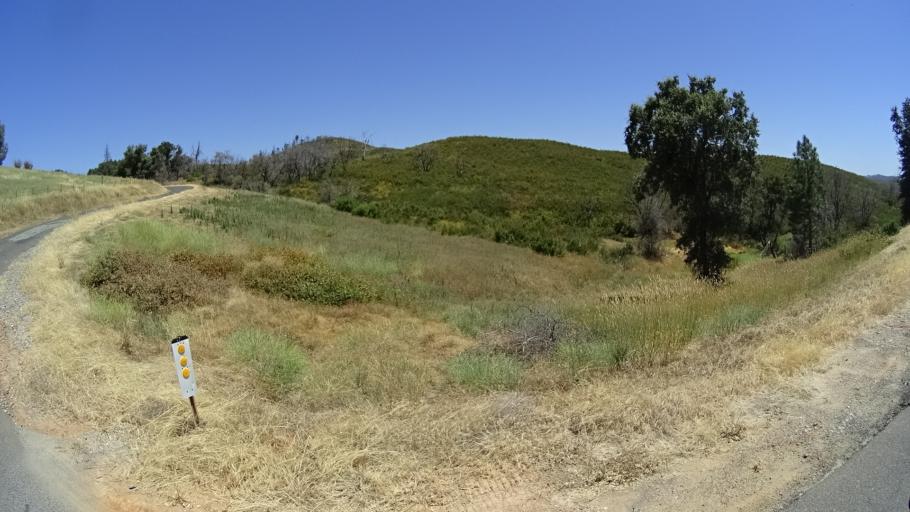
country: US
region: California
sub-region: Calaveras County
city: Mountain Ranch
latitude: 38.2914
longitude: -120.6215
